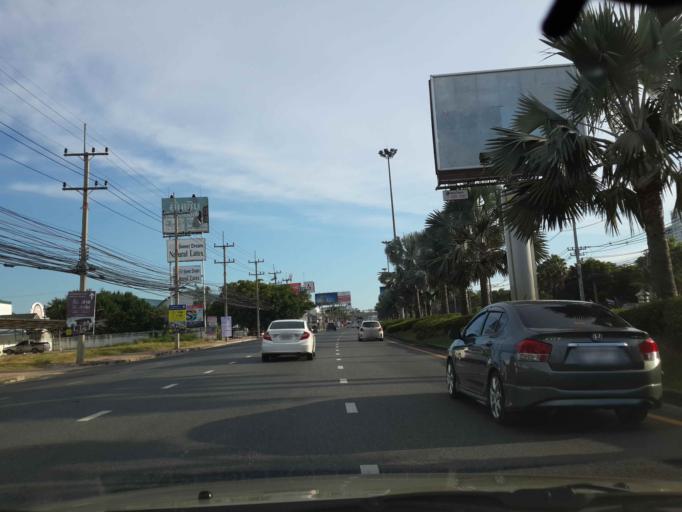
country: TH
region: Chon Buri
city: Bang Lamung
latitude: 12.9884
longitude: 100.9241
